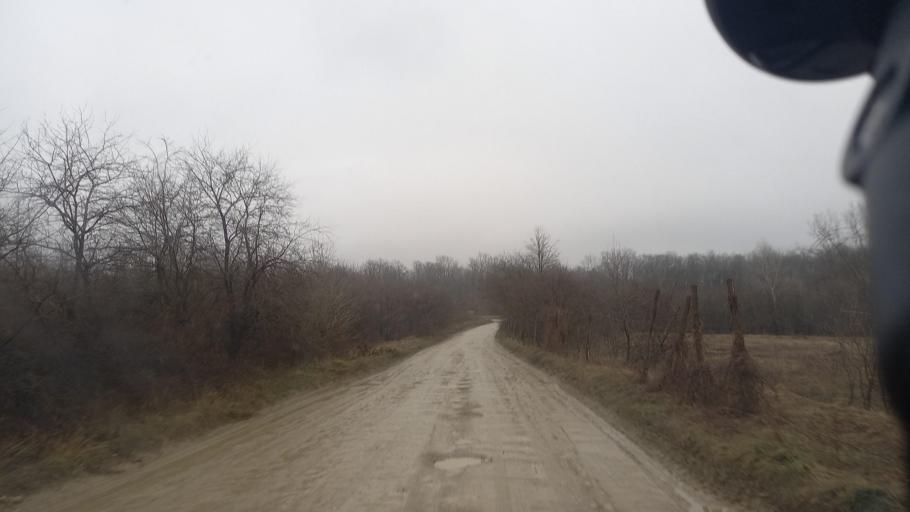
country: RU
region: Krasnodarskiy
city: Saratovskaya
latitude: 44.6660
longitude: 39.2190
